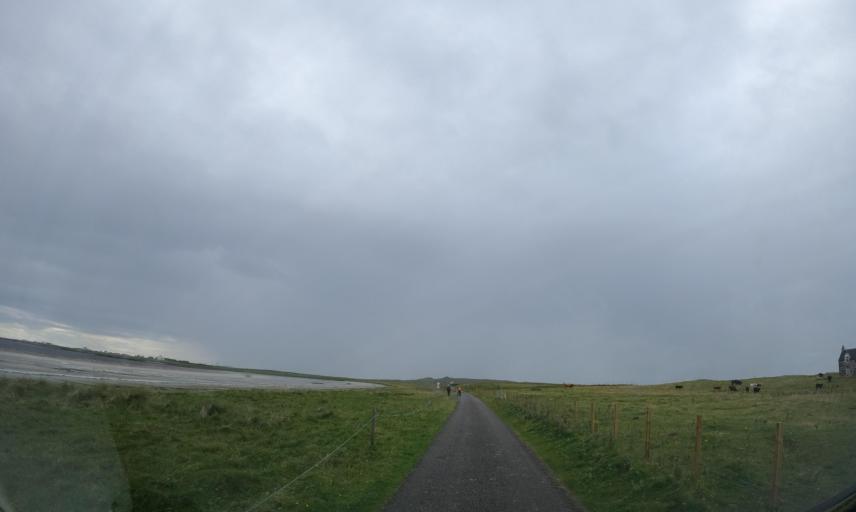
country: GB
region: Scotland
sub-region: Eilean Siar
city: Barra
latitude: 56.5186
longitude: -6.8122
